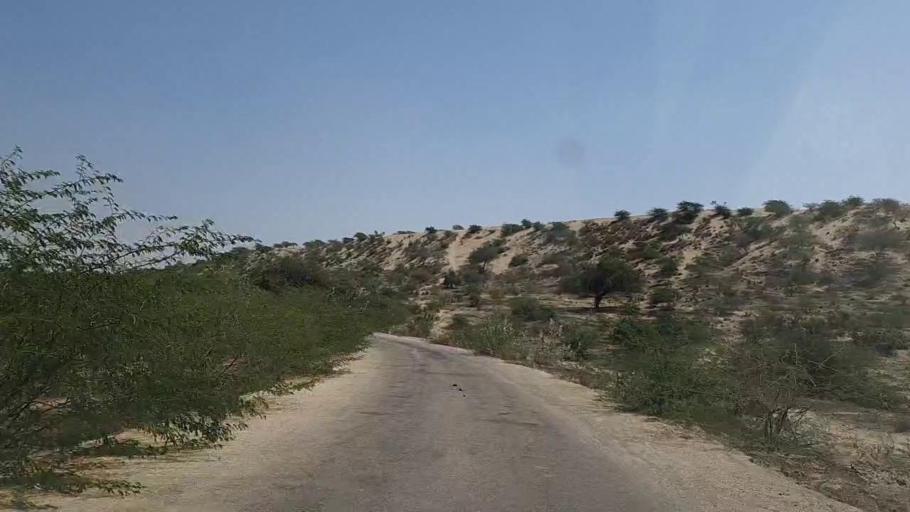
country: PK
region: Sindh
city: Diplo
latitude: 24.4837
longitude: 69.4523
